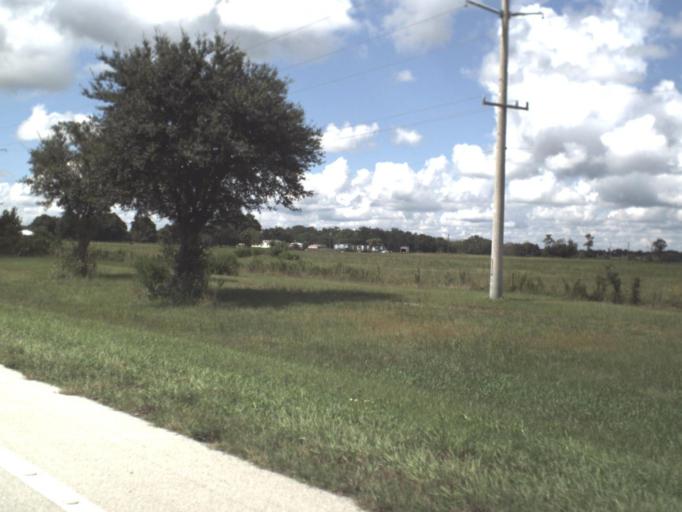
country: US
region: Florida
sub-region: DeSoto County
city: Southeast Arcadia
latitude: 27.2088
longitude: -81.7477
